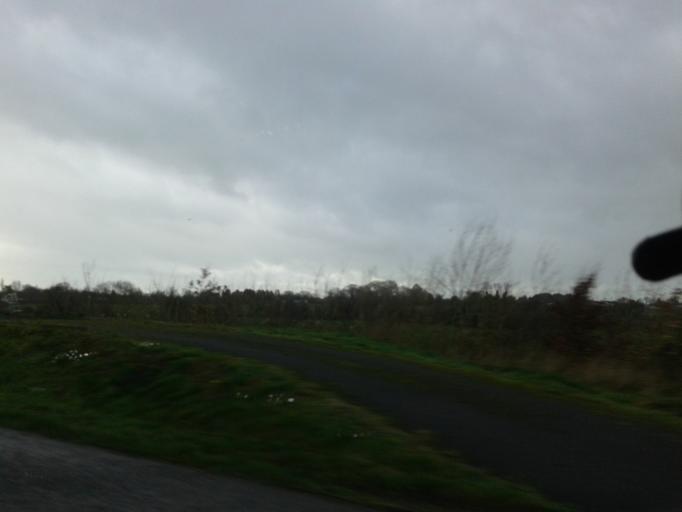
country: IE
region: Leinster
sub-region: An Mhi
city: Ashbourne
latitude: 53.5024
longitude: -6.4186
